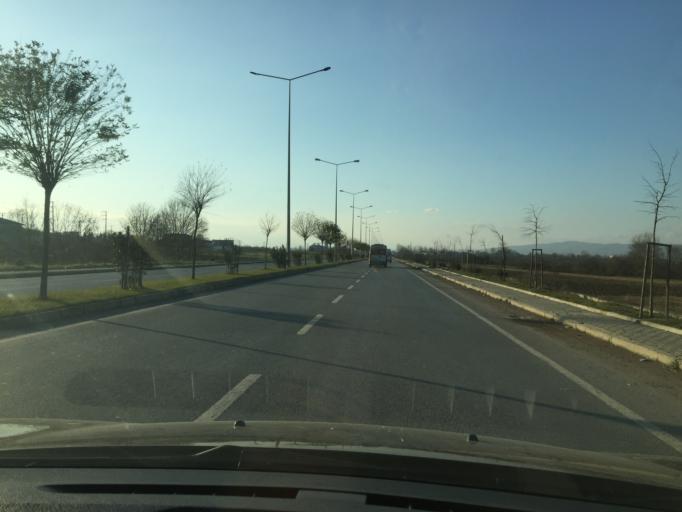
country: TR
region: Sakarya
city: Sogutlu
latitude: 40.9026
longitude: 30.4998
